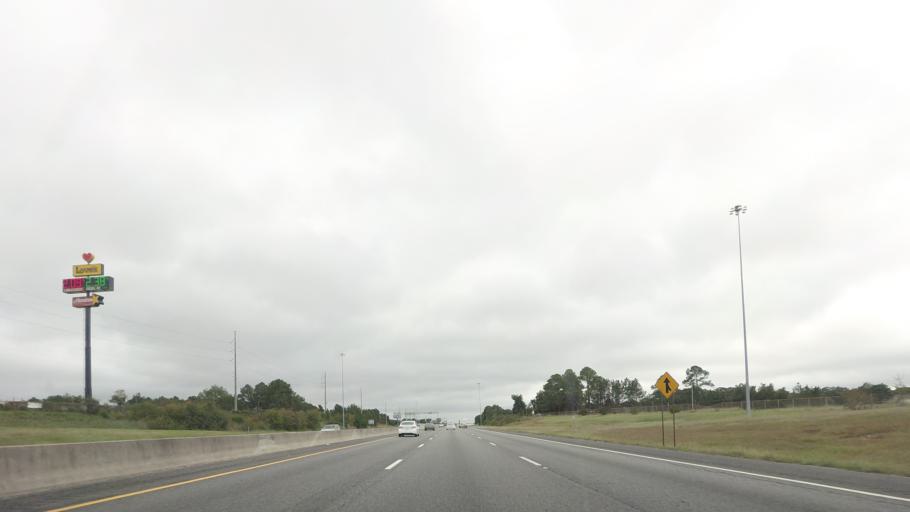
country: US
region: Georgia
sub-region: Tift County
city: Unionville
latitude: 31.4151
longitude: -83.5050
